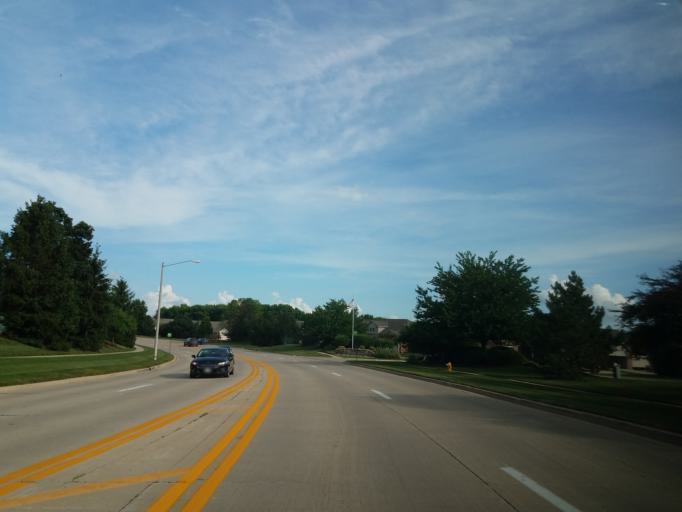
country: US
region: Illinois
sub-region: McLean County
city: Normal
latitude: 40.5063
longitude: -88.9418
